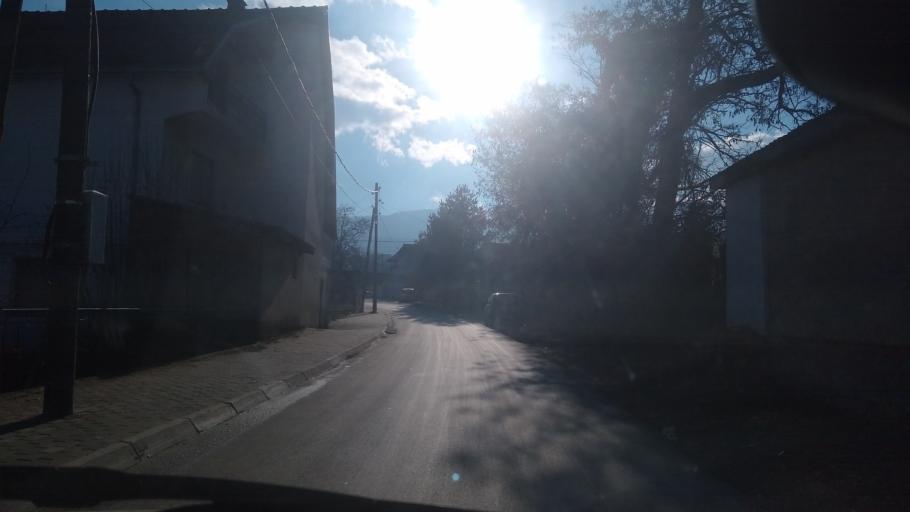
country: MK
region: Bitola
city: Bitola
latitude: 41.0100
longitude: 21.3458
